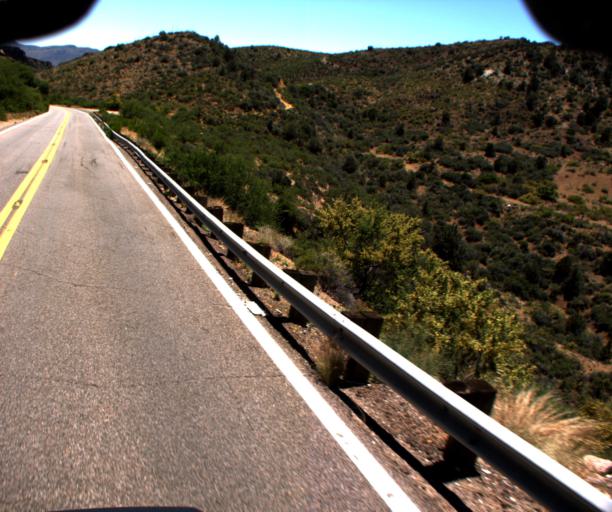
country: US
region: Arizona
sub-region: Pinal County
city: Kearny
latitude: 33.2018
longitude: -110.8039
